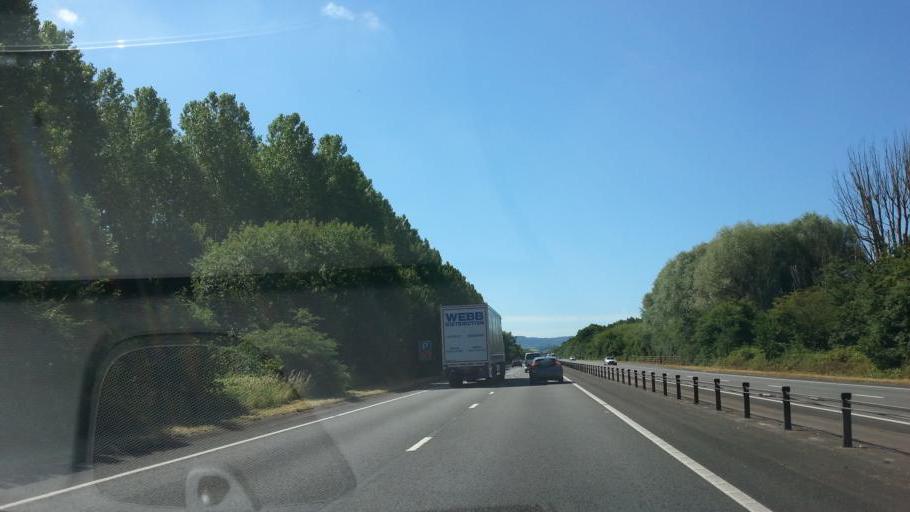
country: GB
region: Wales
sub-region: Monmouthshire
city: Llangwm
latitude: 51.7549
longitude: -2.8423
